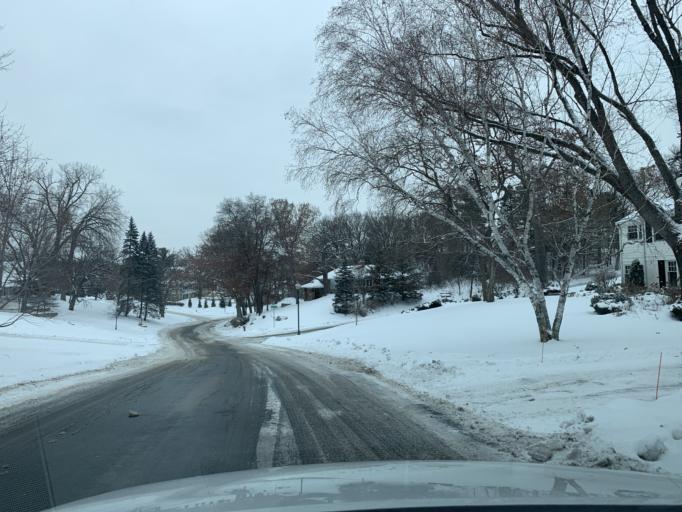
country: US
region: Minnesota
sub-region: Hennepin County
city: Edina
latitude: 44.9117
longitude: -93.3475
